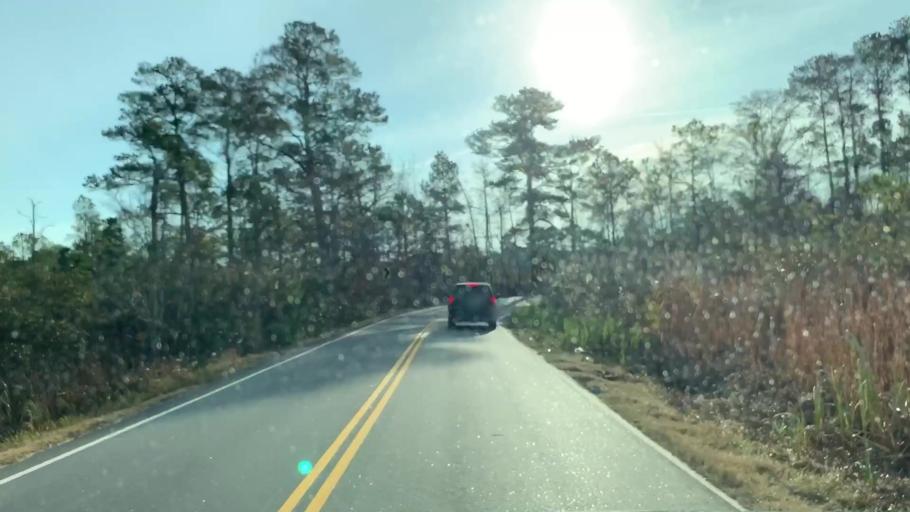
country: US
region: Virginia
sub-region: City of Virginia Beach
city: Virginia Beach
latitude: 36.6938
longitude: -76.0380
